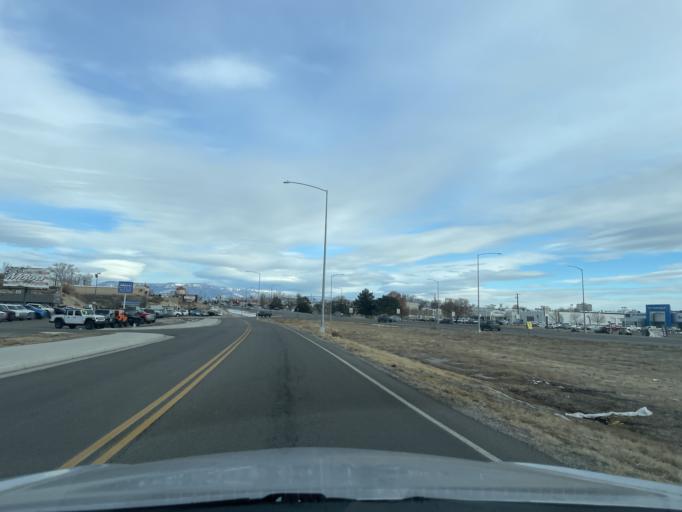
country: US
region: Colorado
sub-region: Mesa County
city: Grand Junction
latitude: 39.0780
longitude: -108.5761
